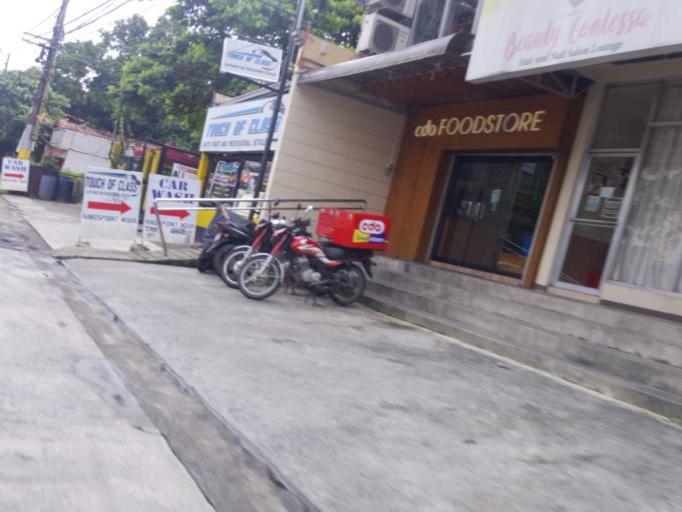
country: PH
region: Calabarzon
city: Bagong Pagasa
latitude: 14.6989
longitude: 121.0235
